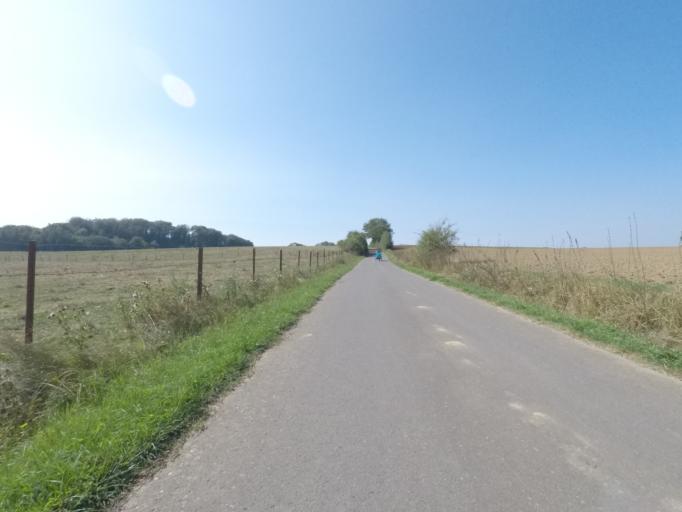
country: LU
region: Luxembourg
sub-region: Canton de Capellen
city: Mamer
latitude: 49.6485
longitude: 6.0215
